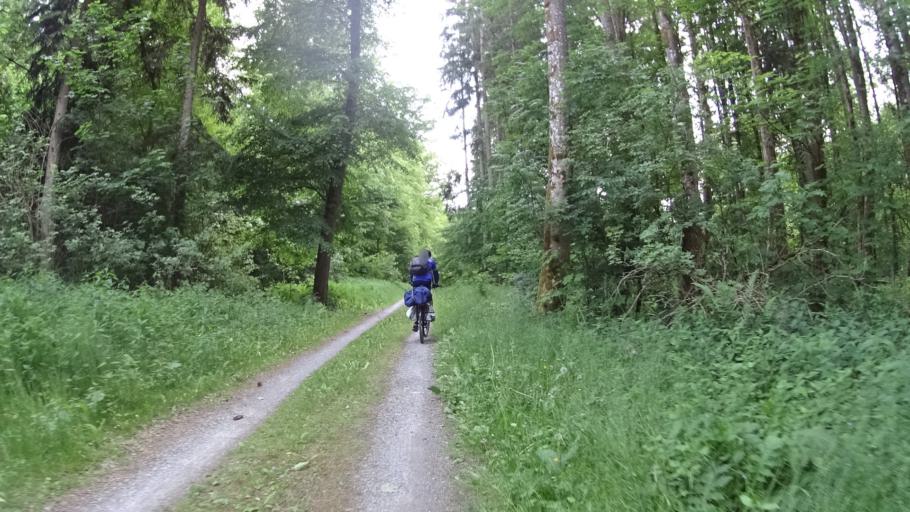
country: DE
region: Baden-Wuerttemberg
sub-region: Karlsruhe Region
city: Hopfingen
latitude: 49.6462
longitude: 9.4329
